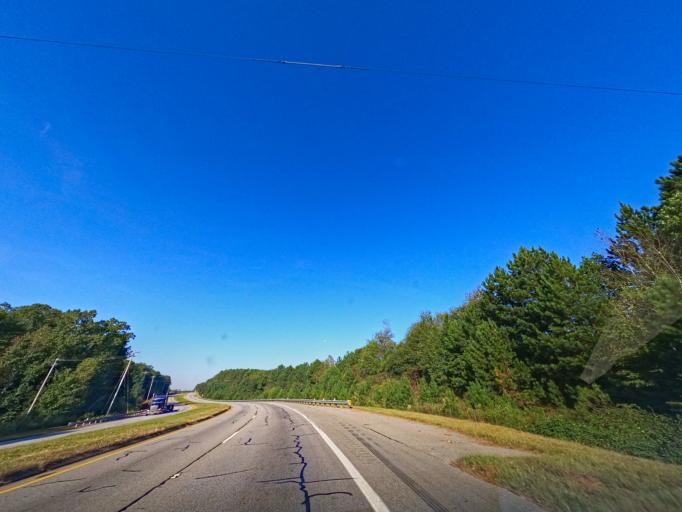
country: US
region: Georgia
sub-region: Coweta County
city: Newnan
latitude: 33.4015
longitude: -84.7993
